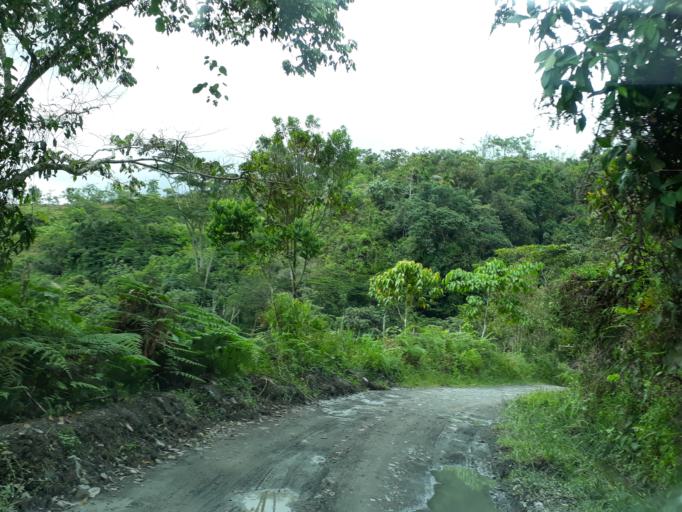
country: CO
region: Boyaca
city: Quipama
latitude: 5.3973
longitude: -74.1261
